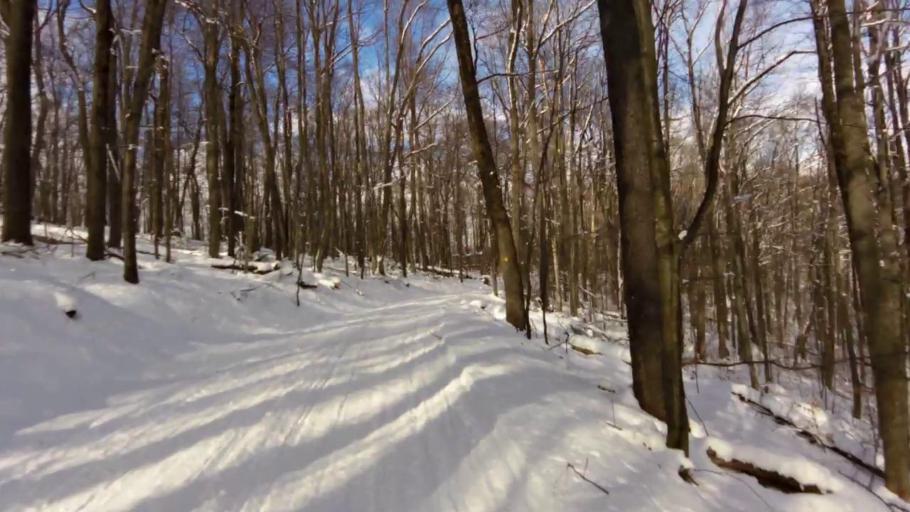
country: US
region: New York
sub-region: Cattaraugus County
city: Salamanca
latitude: 42.0633
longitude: -78.6962
